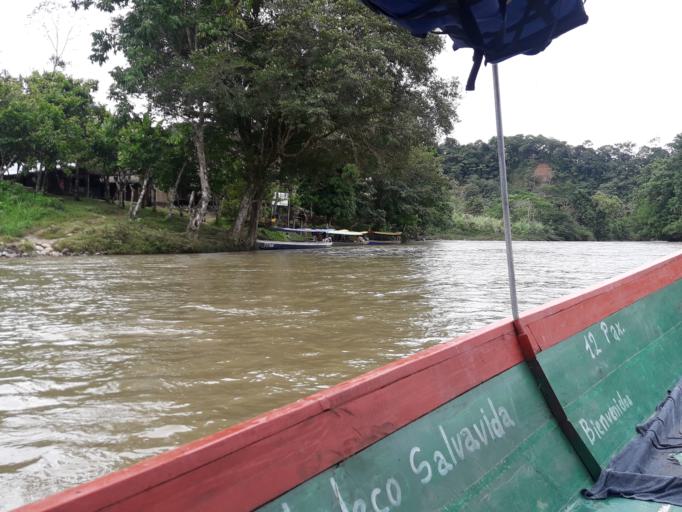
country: EC
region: Napo
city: Tena
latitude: -1.0371
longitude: -77.6568
